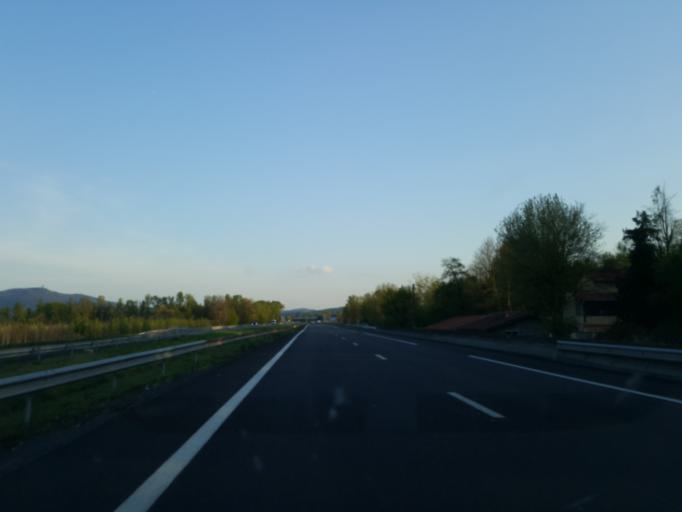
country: FR
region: Rhone-Alpes
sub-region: Departement du Rhone
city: Anse
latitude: 45.9126
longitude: 4.7270
